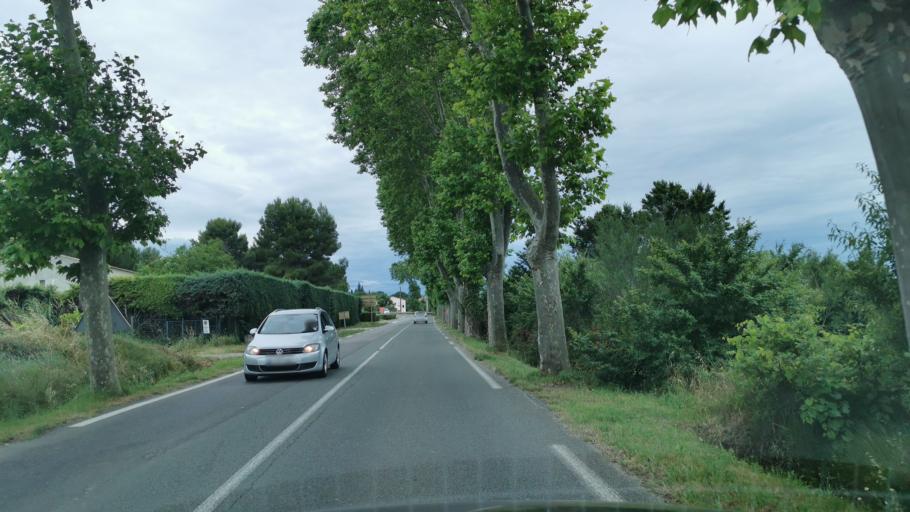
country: FR
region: Languedoc-Roussillon
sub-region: Departement de l'Aude
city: Marcorignan
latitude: 43.2318
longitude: 2.9254
